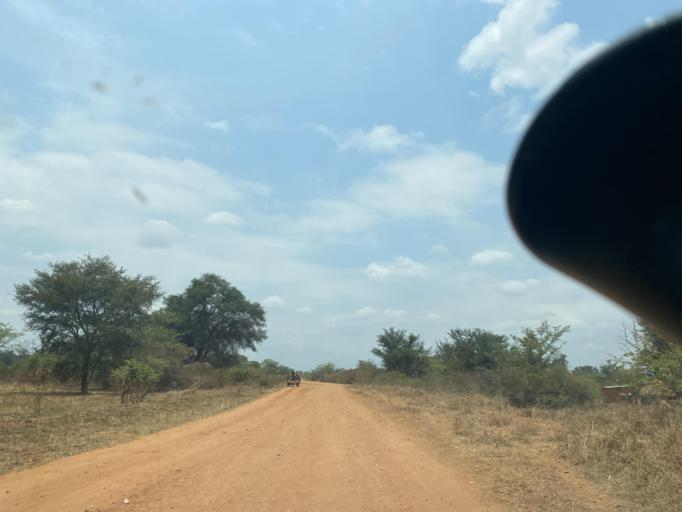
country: ZM
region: Lusaka
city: Chongwe
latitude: -15.5151
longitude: 28.8193
